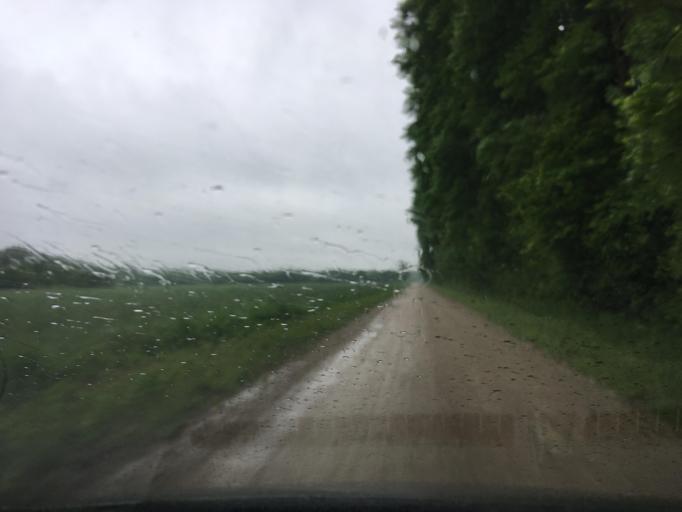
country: EE
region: Laeaene
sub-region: Lihula vald
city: Lihula
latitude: 58.6281
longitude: 23.8160
